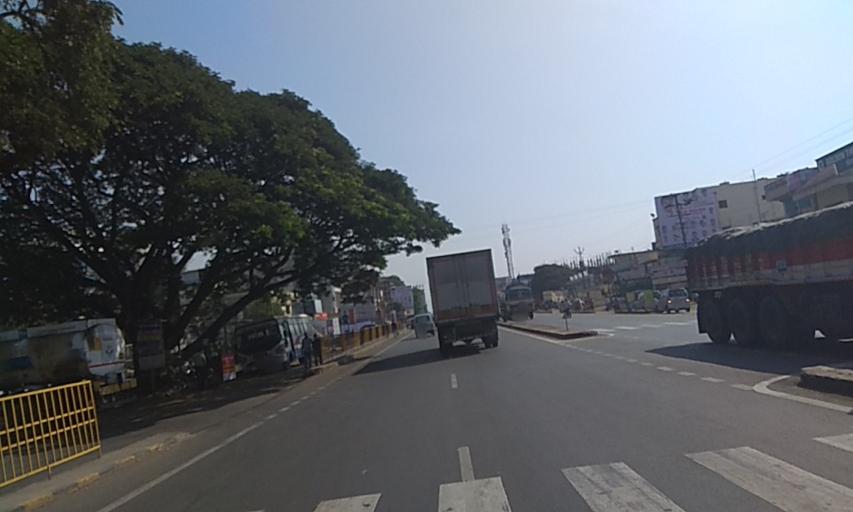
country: IN
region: Maharashtra
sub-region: Pune Division
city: Lohogaon
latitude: 18.4896
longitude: 74.0183
